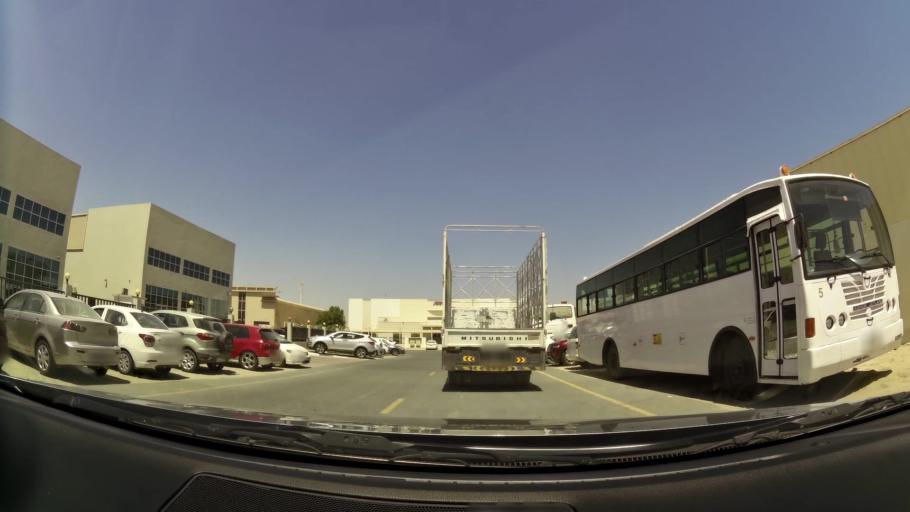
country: AE
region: Dubai
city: Dubai
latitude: 24.9871
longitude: 55.1944
